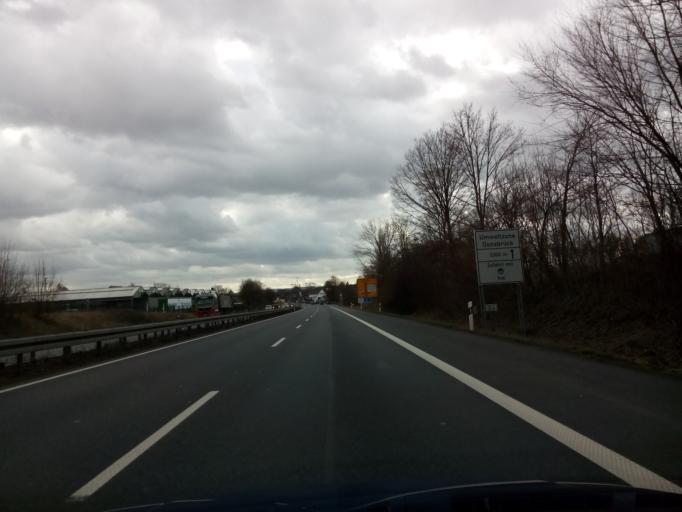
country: DE
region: Lower Saxony
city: Osnabrueck
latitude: 52.3063
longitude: 8.0344
